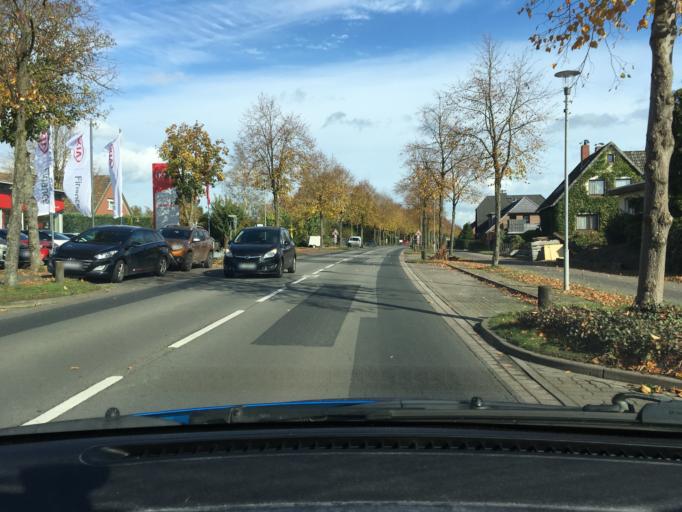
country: DE
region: Lower Saxony
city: Wistedt
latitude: 53.2785
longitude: 9.6949
